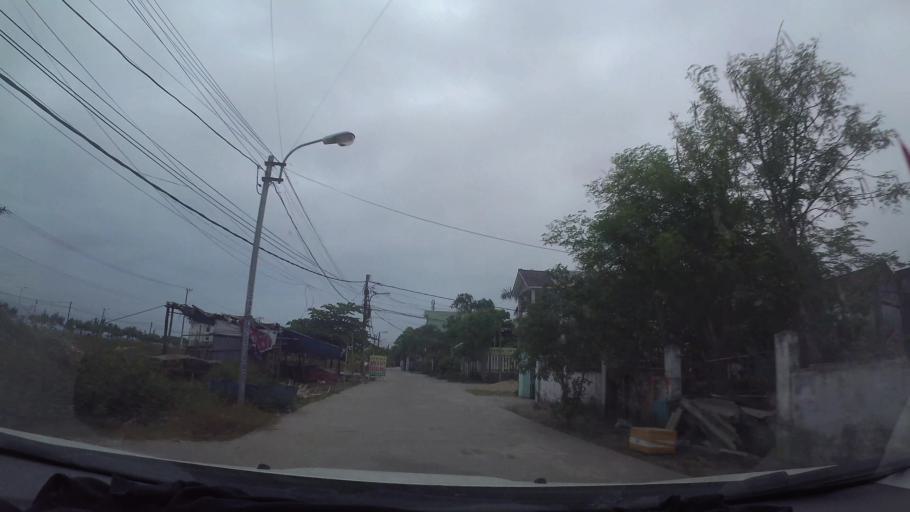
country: VN
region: Da Nang
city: Lien Chieu
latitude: 16.0857
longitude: 108.1569
